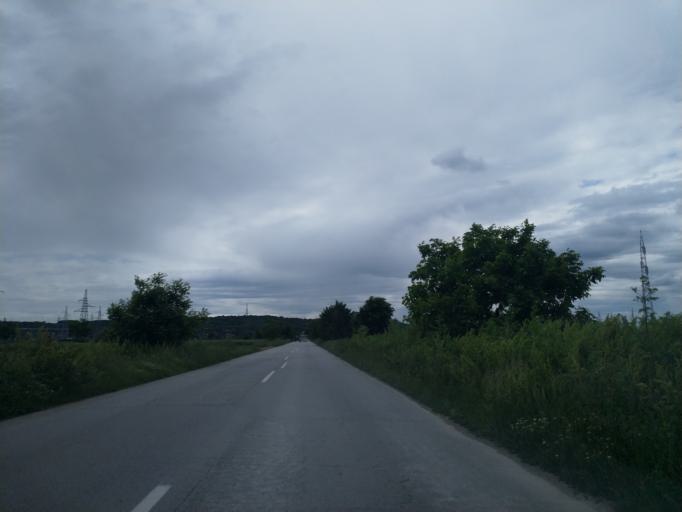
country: RS
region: Central Serbia
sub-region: Pomoravski Okrug
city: Jagodina
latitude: 43.9560
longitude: 21.3013
